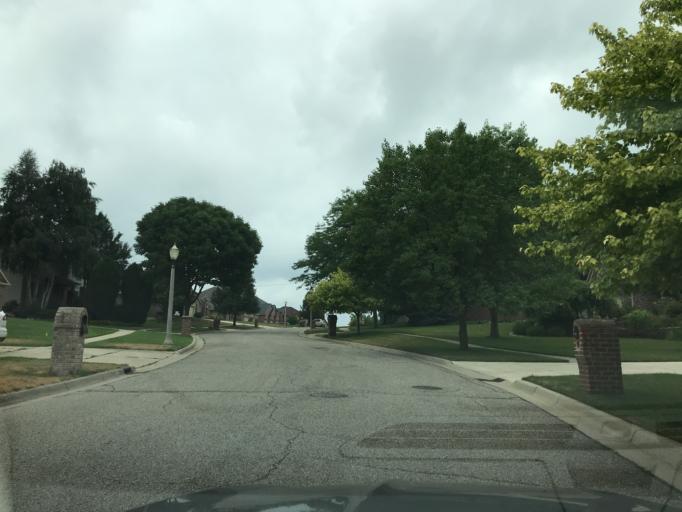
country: US
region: Michigan
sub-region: Eaton County
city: Waverly
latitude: 42.7594
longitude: -84.6312
